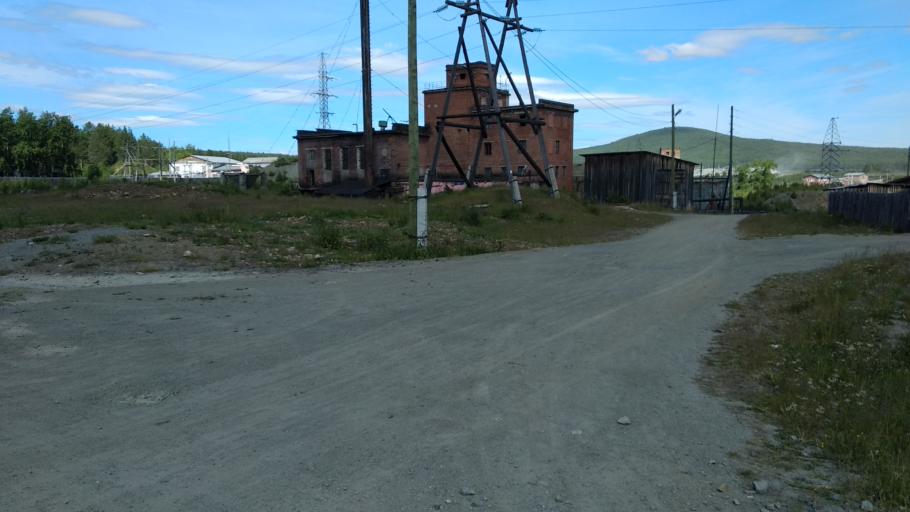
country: RU
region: Sverdlovsk
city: Severoural'sk
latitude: 60.1423
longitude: 59.8230
